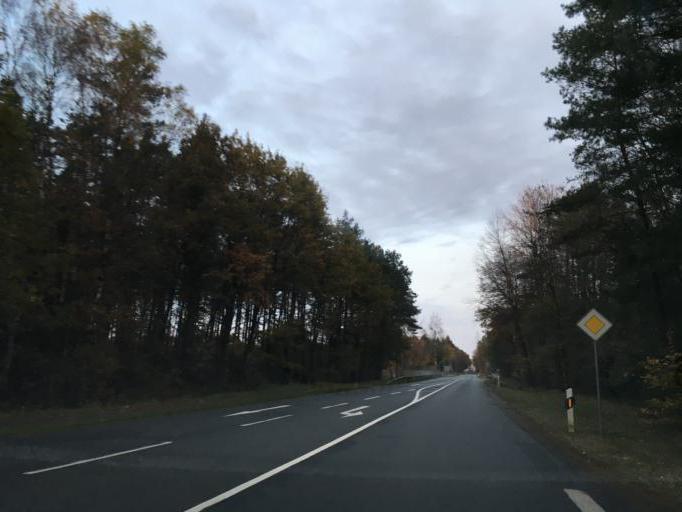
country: DE
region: Lower Saxony
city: Bispingen
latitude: 53.0709
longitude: 9.9707
